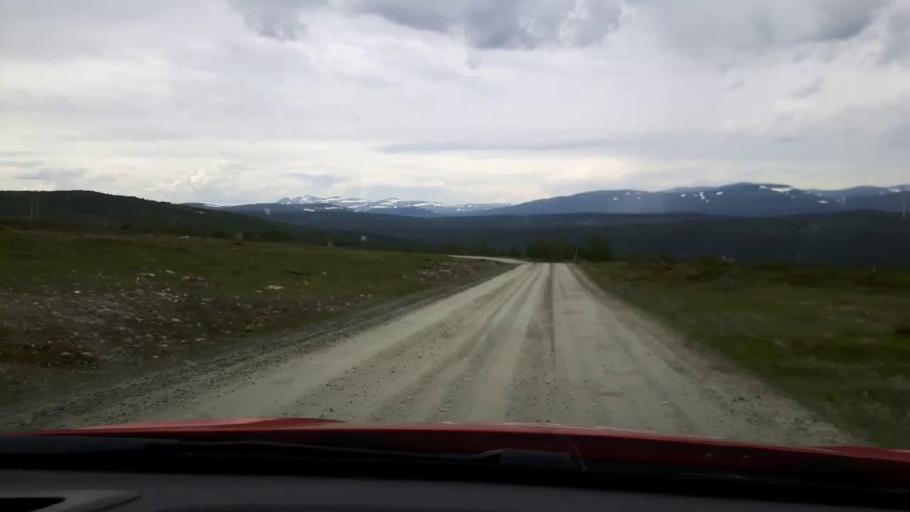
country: SE
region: Jaemtland
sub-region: Are Kommun
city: Are
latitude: 62.7812
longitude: 12.7658
